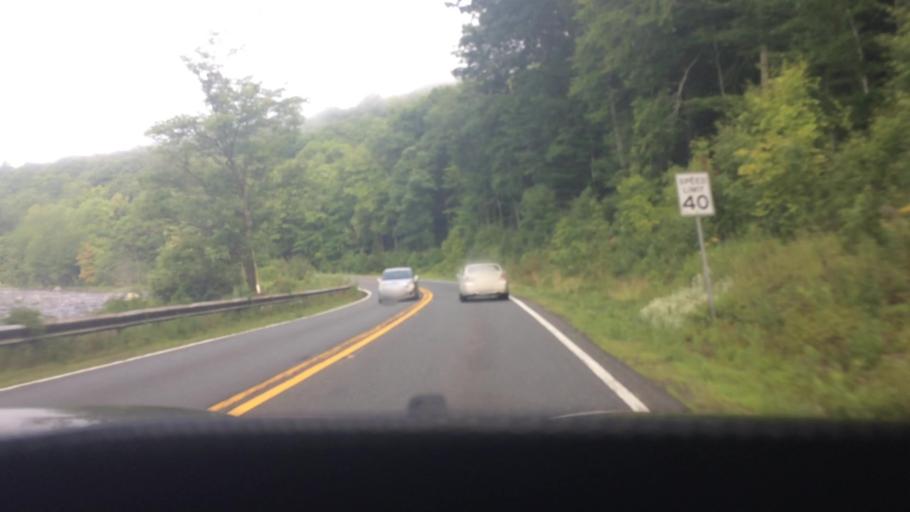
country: US
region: Massachusetts
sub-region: Franklin County
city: Erving
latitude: 42.6080
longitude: -72.4249
